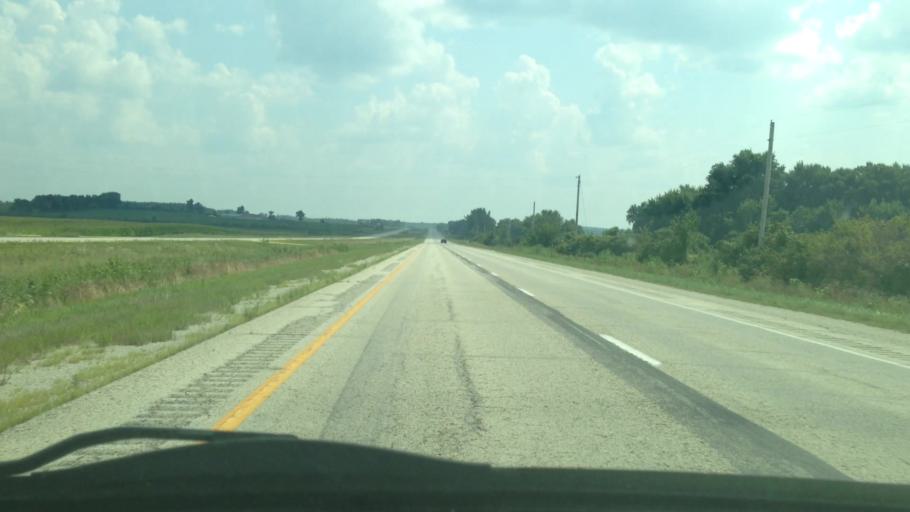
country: US
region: Iowa
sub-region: Chickasaw County
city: New Hampton
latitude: 42.9282
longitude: -92.3176
